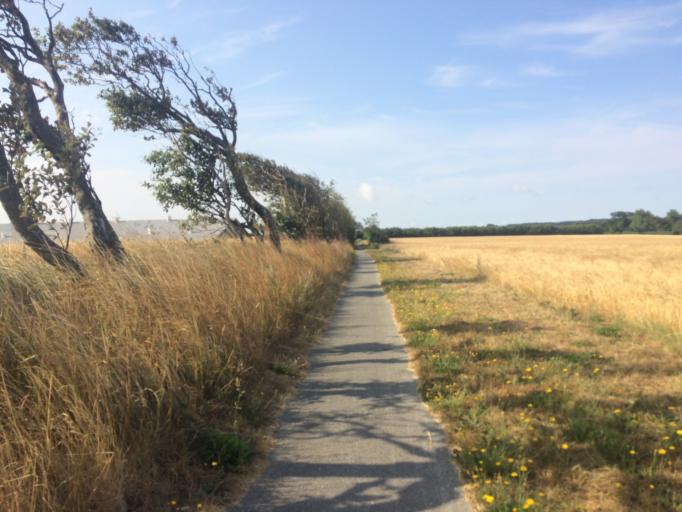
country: DK
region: Central Jutland
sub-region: Holstebro Kommune
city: Vinderup
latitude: 56.6298
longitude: 8.7843
